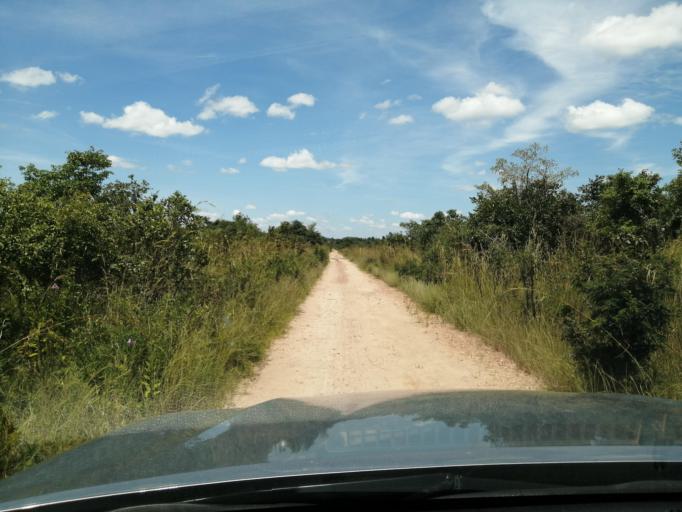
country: ZM
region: Central
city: Chibombo
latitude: -15.1132
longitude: 27.8572
